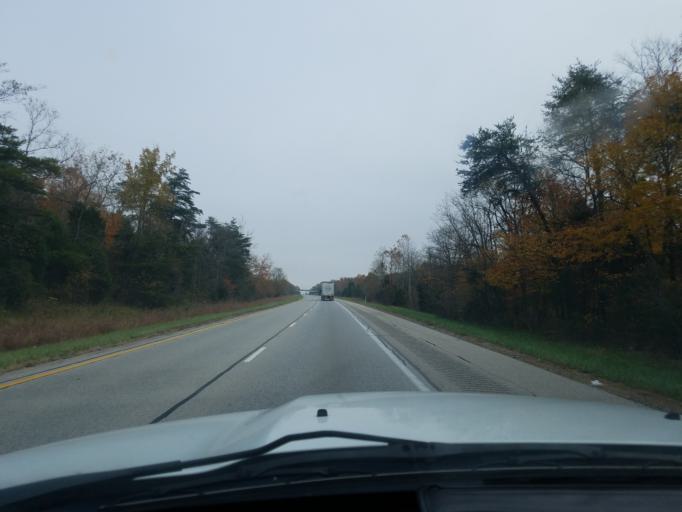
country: US
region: Indiana
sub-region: Floyd County
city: Georgetown
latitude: 38.2739
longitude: -85.9626
